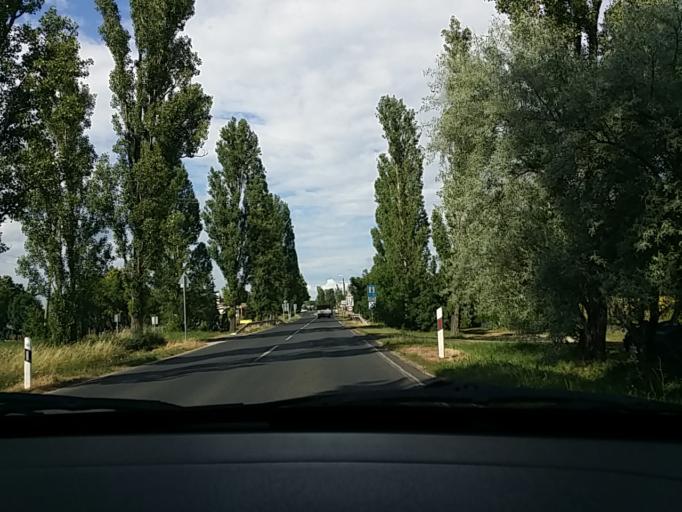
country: HU
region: Veszprem
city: Zanka
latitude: 46.8704
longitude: 17.6812
